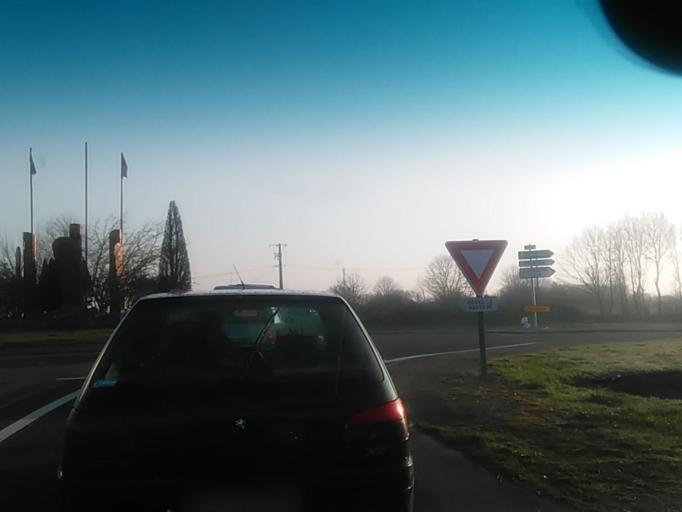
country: FR
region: Lower Normandy
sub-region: Departement du Calvados
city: Falaise
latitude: 48.8820
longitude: -0.2071
